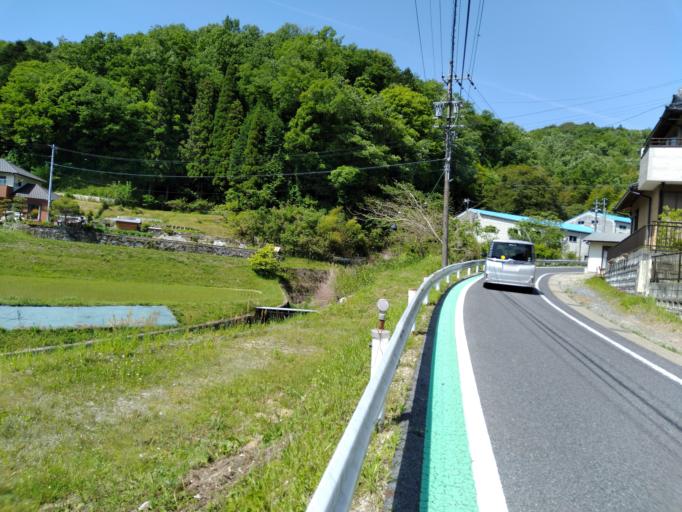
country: JP
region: Gifu
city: Toki
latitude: 35.2438
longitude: 137.2242
